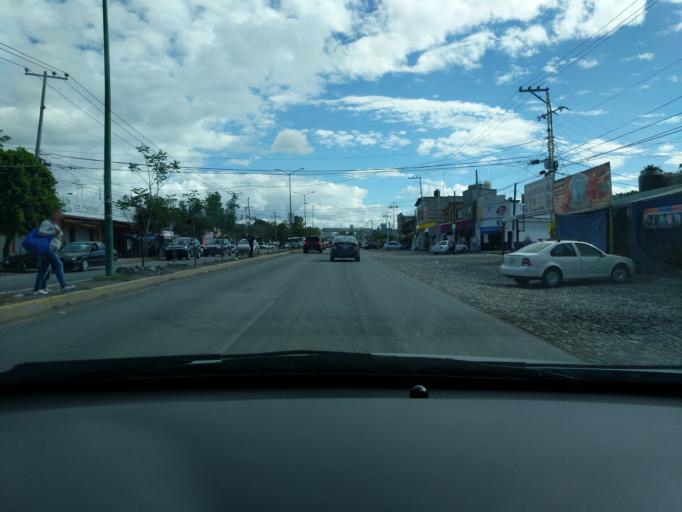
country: MX
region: Queretaro
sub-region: El Marques
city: General Lazaro Cardenas (El Colorado)
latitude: 20.5789
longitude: -100.2555
